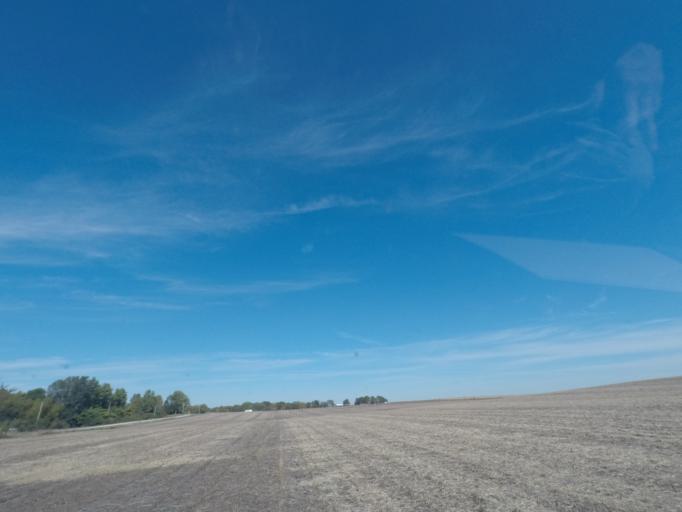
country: US
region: Iowa
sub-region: Story County
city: Nevada
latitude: 42.0372
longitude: -93.3613
